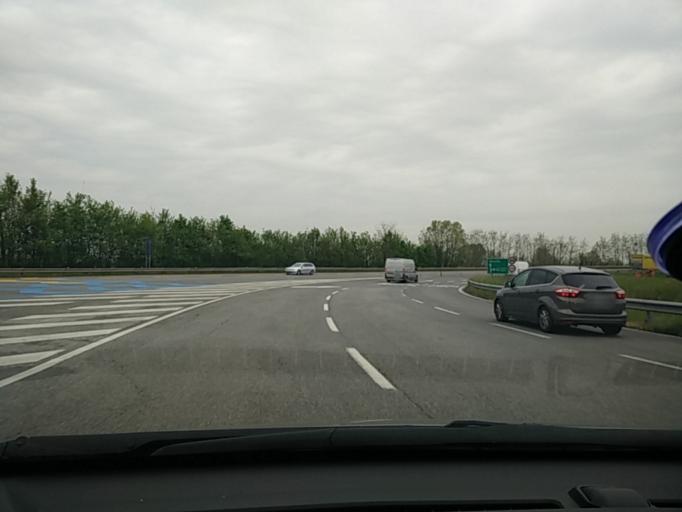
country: IT
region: Veneto
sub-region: Provincia di Treviso
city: Lancenigo-Villorba
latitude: 45.7213
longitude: 12.2843
